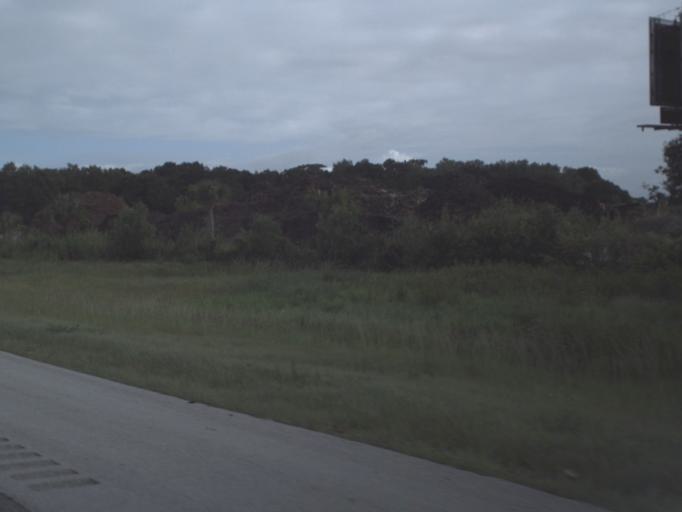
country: US
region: Florida
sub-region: Lee County
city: Suncoast Estates
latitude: 26.7228
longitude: -81.8255
